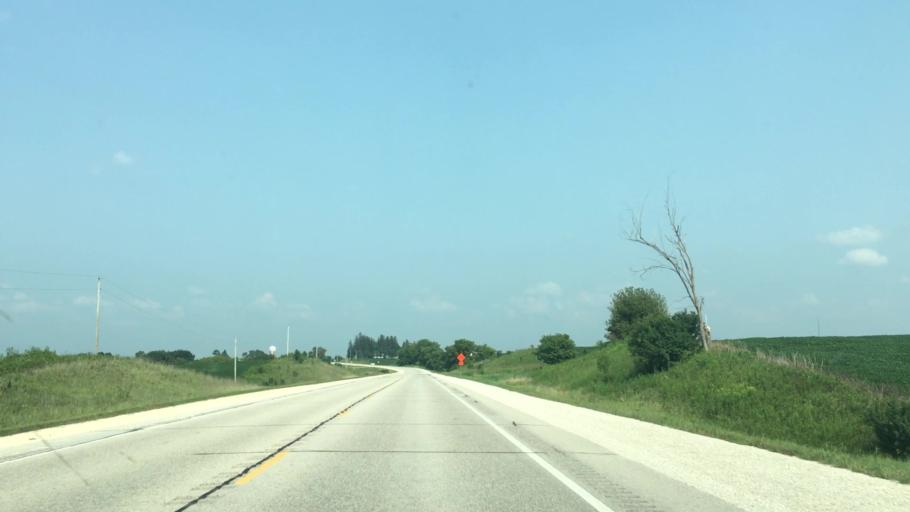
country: US
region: Iowa
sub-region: Winneshiek County
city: Decorah
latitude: 43.2755
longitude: -91.8197
